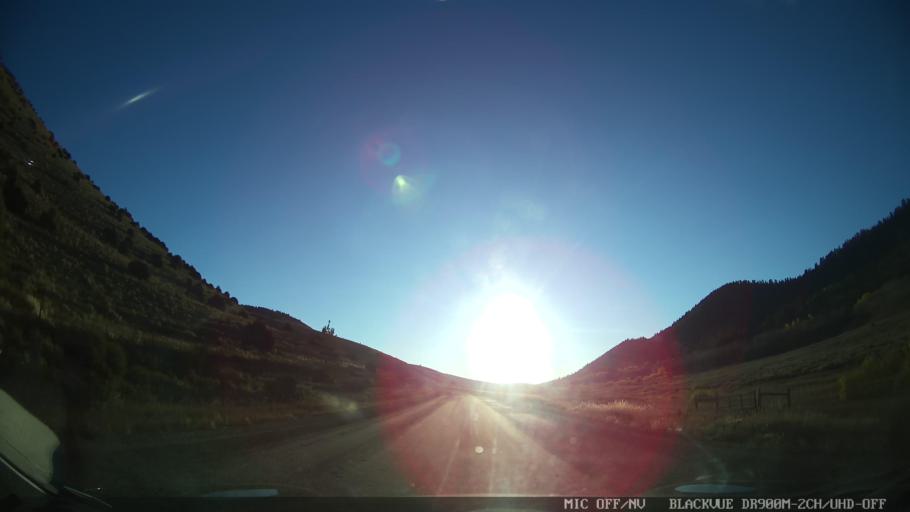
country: US
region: Colorado
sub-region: Grand County
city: Kremmling
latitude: 39.9934
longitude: -106.4668
